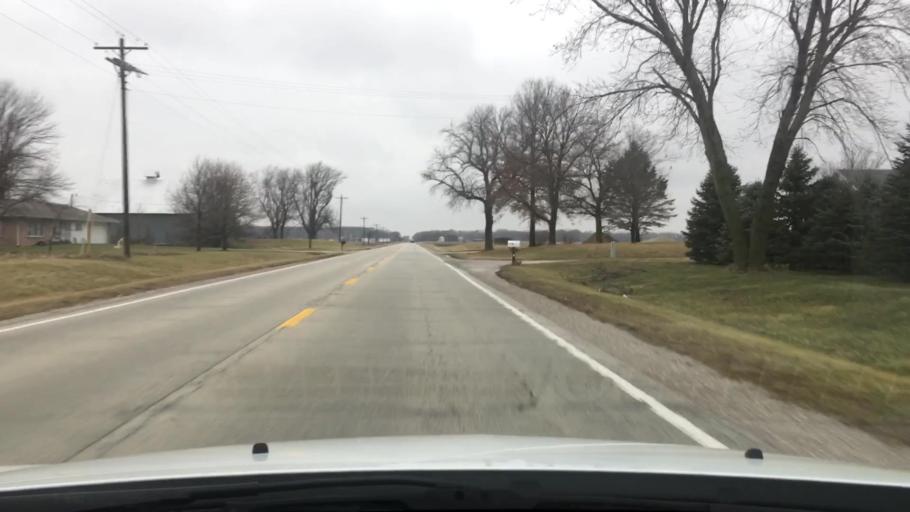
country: US
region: Illinois
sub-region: Iroquois County
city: Clifton
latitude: 40.8882
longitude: -87.8135
